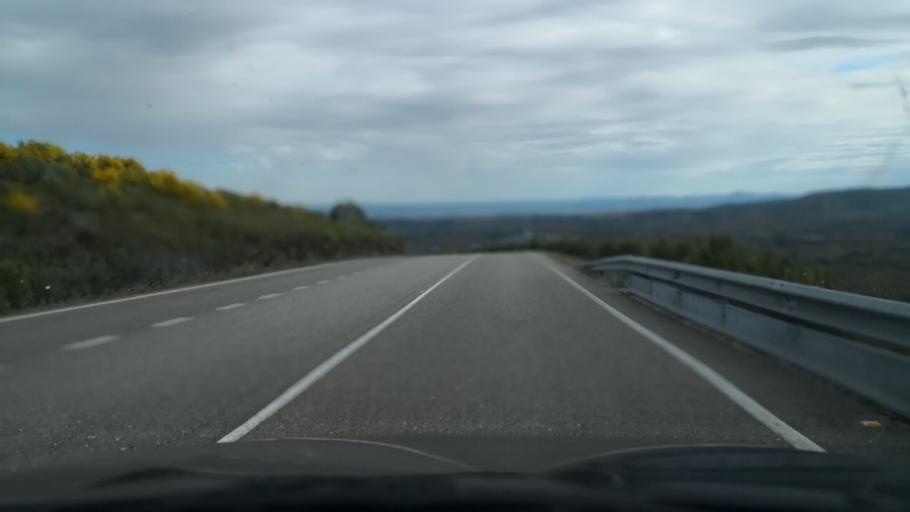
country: ES
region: Extremadura
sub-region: Provincia de Caceres
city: Acebo
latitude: 40.2097
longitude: -6.6764
